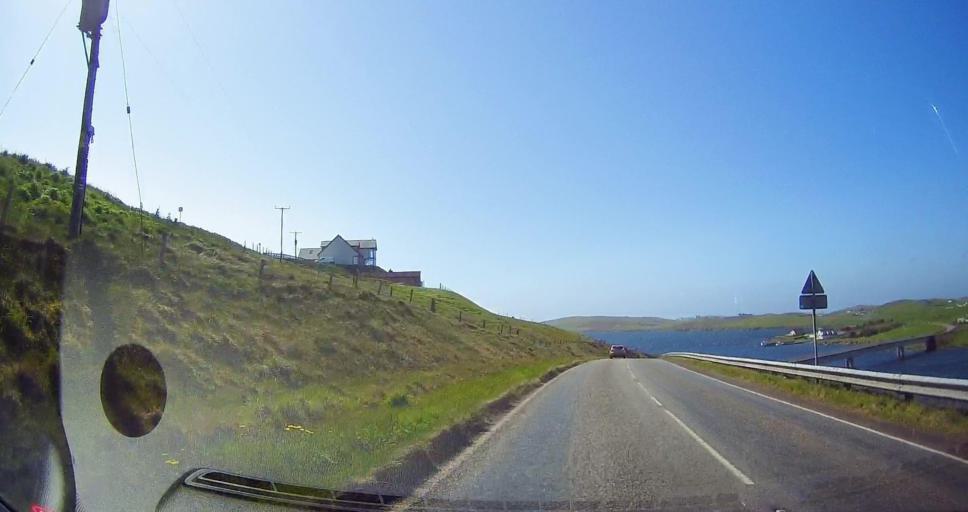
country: GB
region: Scotland
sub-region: Shetland Islands
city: Lerwick
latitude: 60.1309
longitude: -1.2678
